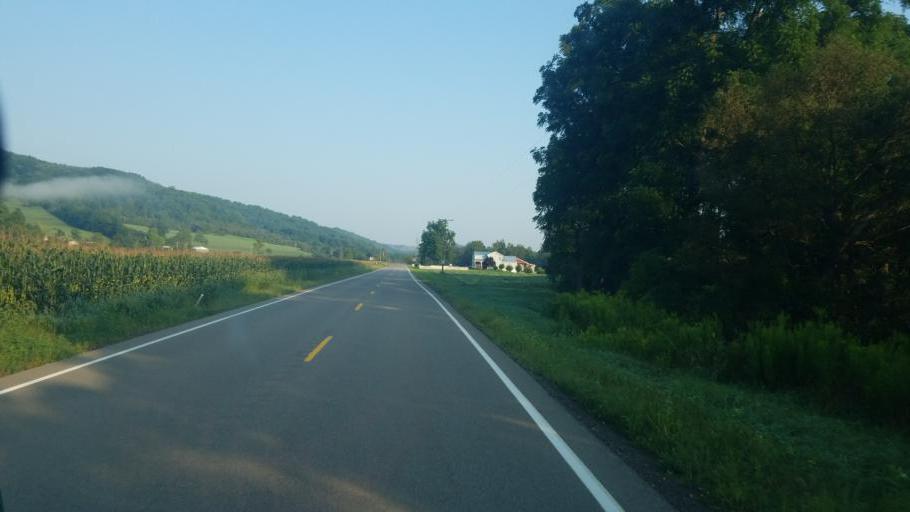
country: US
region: Pennsylvania
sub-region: Tioga County
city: Westfield
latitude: 41.9831
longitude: -77.4766
